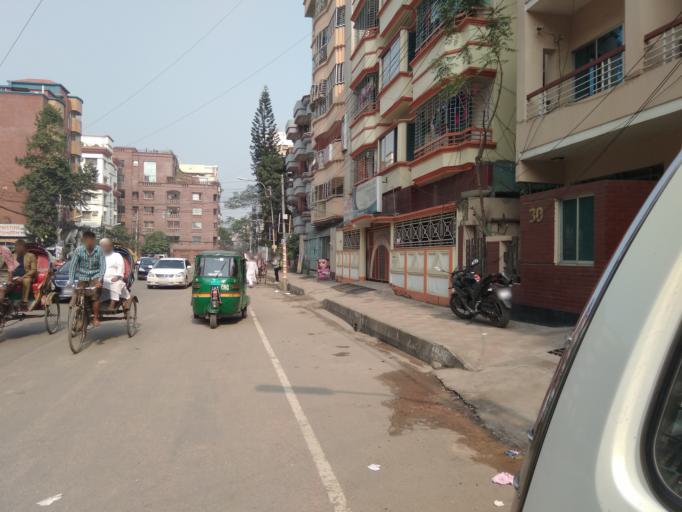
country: BD
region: Dhaka
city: Tungi
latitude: 23.8690
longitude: 90.3939
